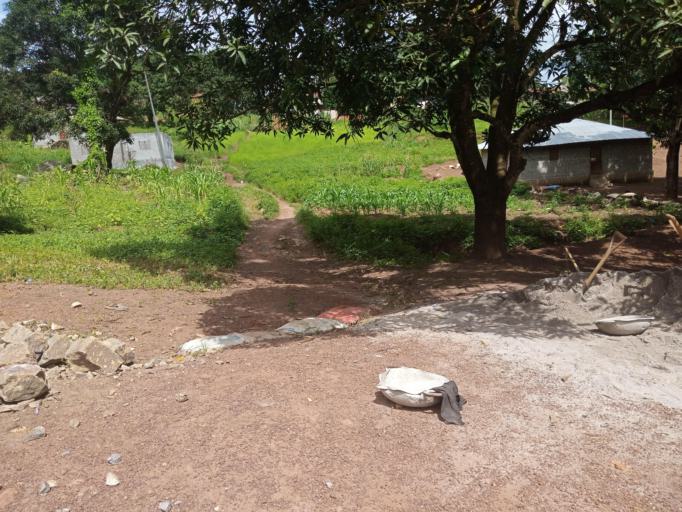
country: SL
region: Northern Province
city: Kamakwie
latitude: 9.4944
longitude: -12.2405
